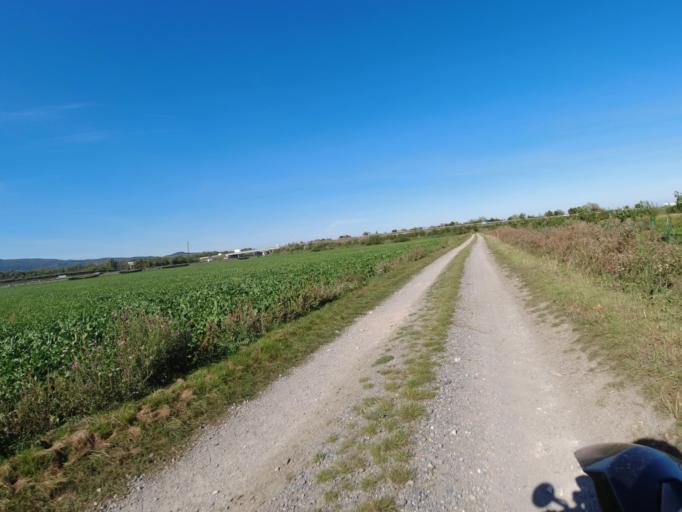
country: AT
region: Lower Austria
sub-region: Politischer Bezirk Modling
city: Guntramsdorf
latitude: 48.0263
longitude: 16.3391
